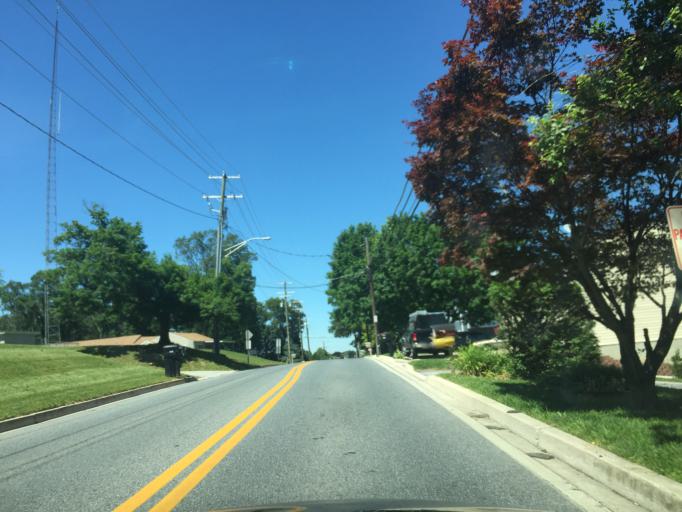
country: US
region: Maryland
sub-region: Carroll County
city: Manchester
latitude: 39.6674
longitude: -76.8781
